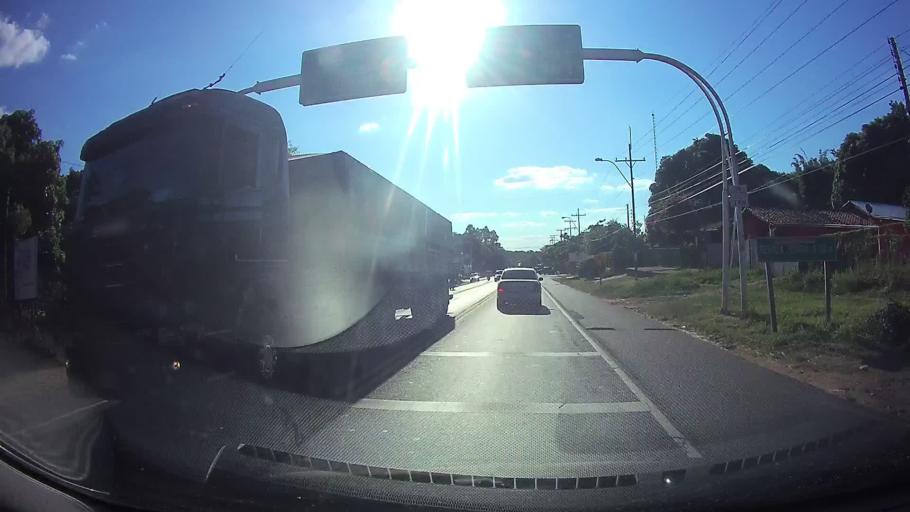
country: PY
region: Central
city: Ypacarai
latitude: -25.3727
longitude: -57.2190
